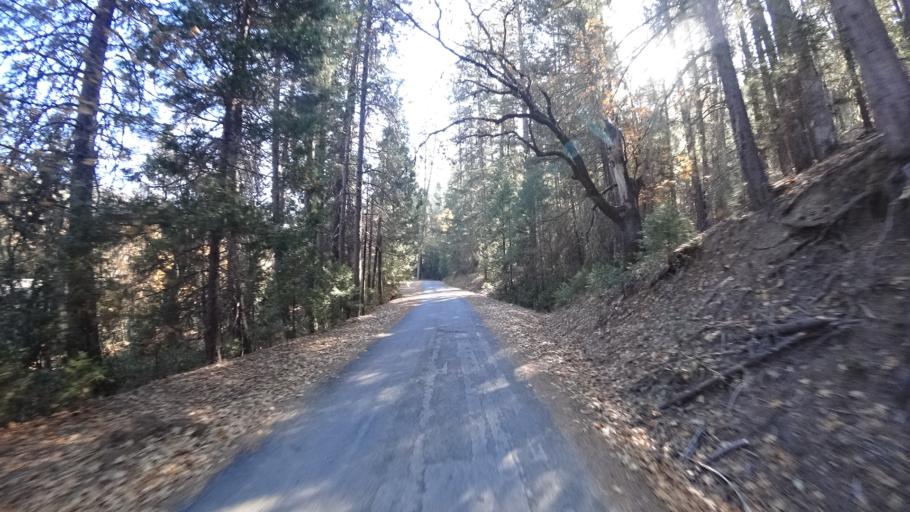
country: US
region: California
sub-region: Siskiyou County
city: Yreka
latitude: 41.8406
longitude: -122.8785
